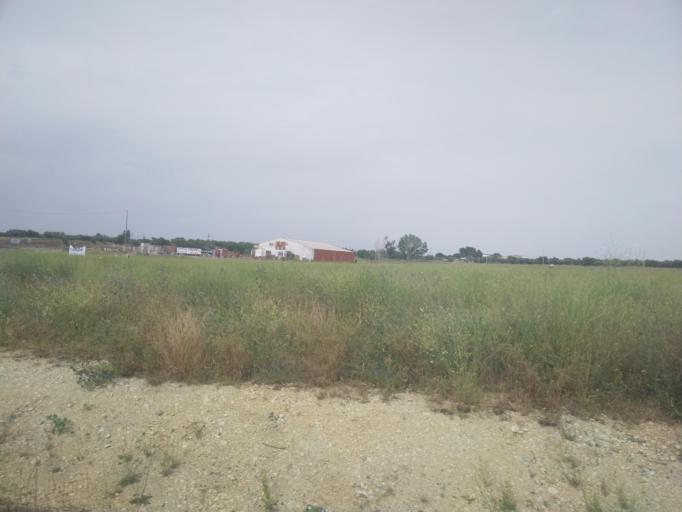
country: ES
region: Castille-La Mancha
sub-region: Province of Toledo
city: Polan
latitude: 39.7838
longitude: -4.1594
